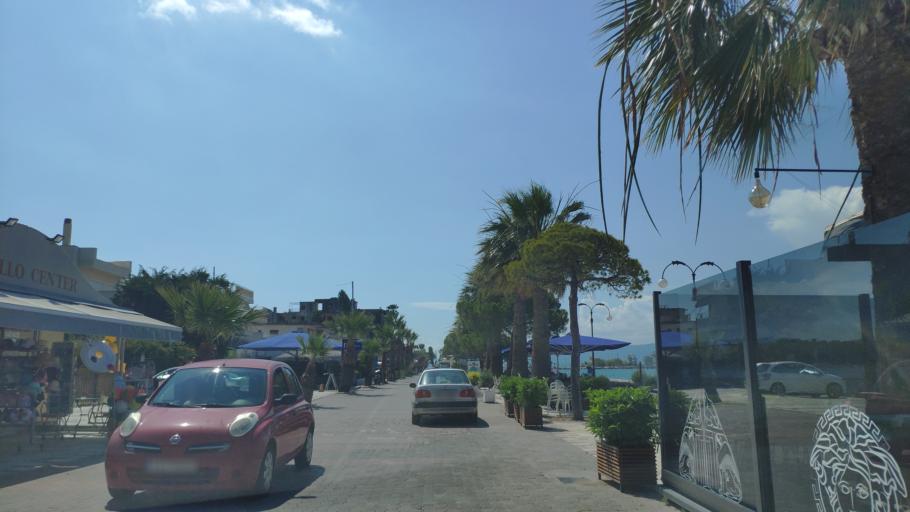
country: GR
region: Central Greece
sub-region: Nomos Evvoias
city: Eretria
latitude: 38.3908
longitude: 23.7975
